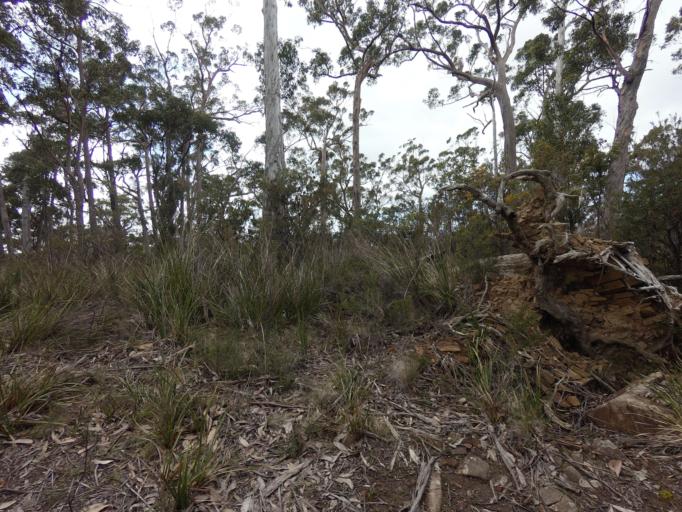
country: AU
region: Tasmania
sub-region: Huon Valley
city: Geeveston
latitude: -43.4779
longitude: 146.9340
